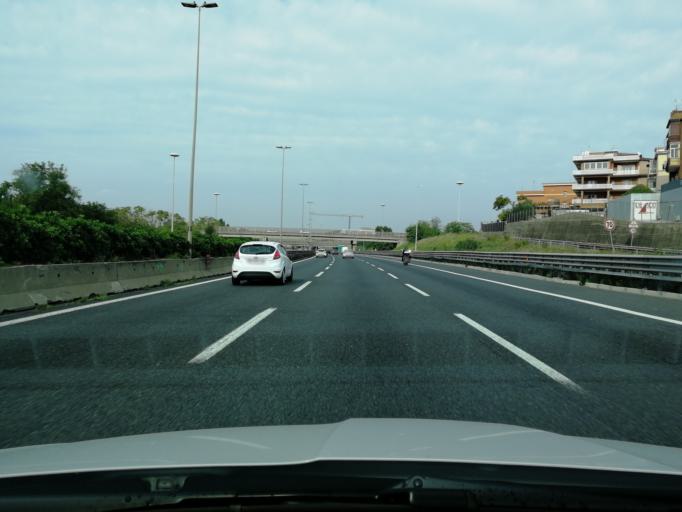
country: IT
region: Latium
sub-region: Citta metropolitana di Roma Capitale
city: Setteville
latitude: 41.8884
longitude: 12.6144
